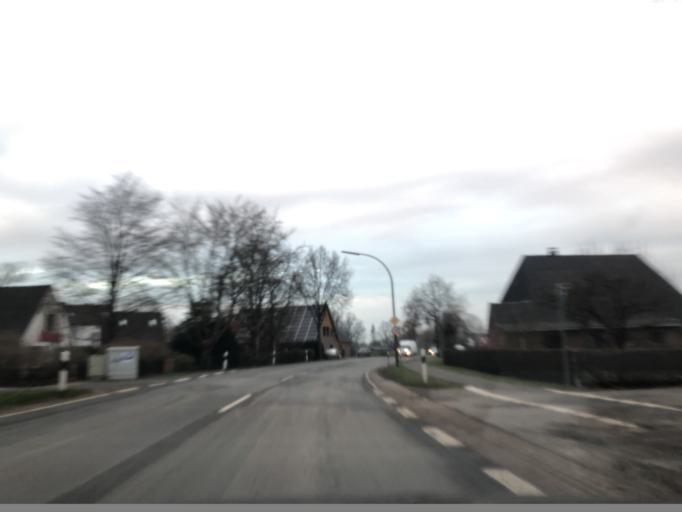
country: DE
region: Lower Saxony
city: Delmenhorst
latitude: 53.0991
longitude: 8.6455
